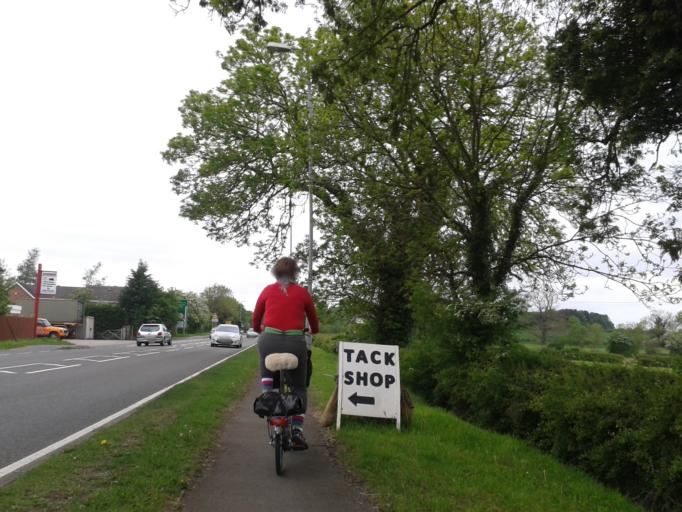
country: GB
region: England
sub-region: Leicestershire
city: Kibworth Harcourt
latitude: 52.5362
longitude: -0.9811
